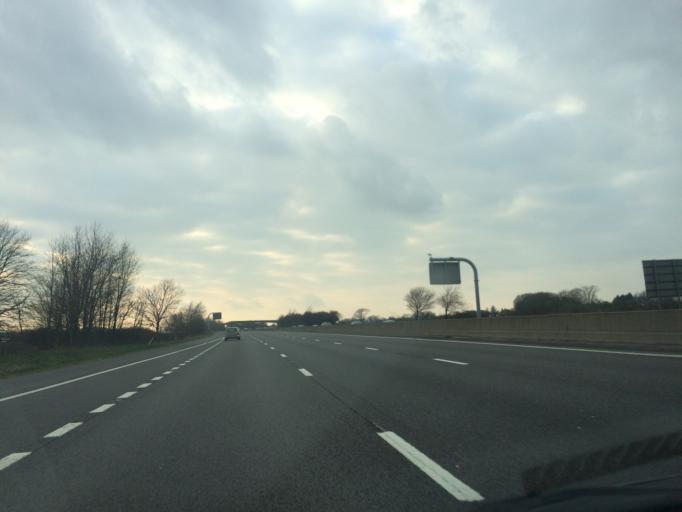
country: GB
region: England
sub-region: West Berkshire
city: Lambourn
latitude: 51.4845
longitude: -1.5636
